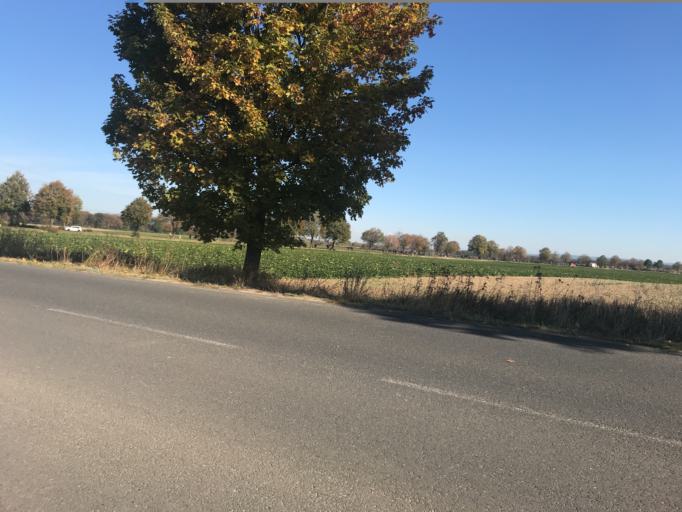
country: DE
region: North Rhine-Westphalia
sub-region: Regierungsbezirk Koln
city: Merzenich
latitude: 50.8654
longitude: 6.5730
